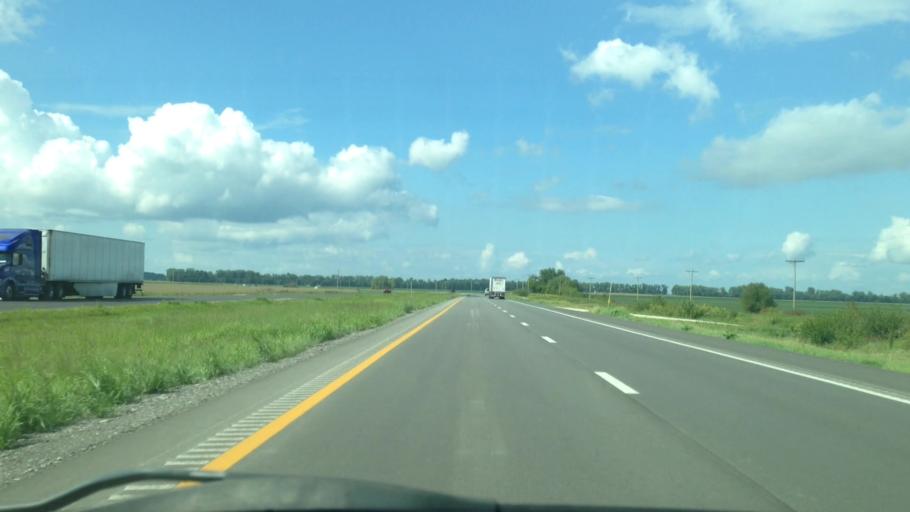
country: US
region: Illinois
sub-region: Adams County
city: Quincy
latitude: 39.9638
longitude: -91.5181
